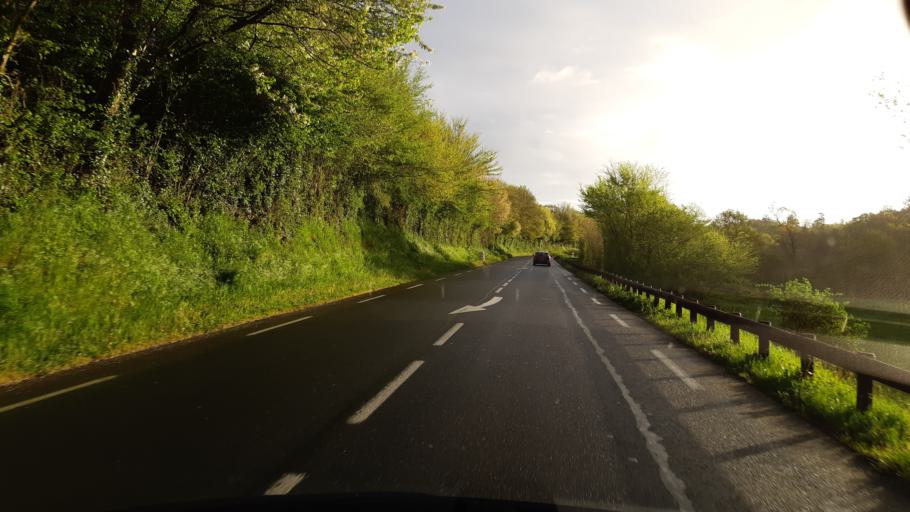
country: FR
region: Lower Normandy
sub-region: Departement de la Manche
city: Agneaux
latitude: 49.0761
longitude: -1.1258
